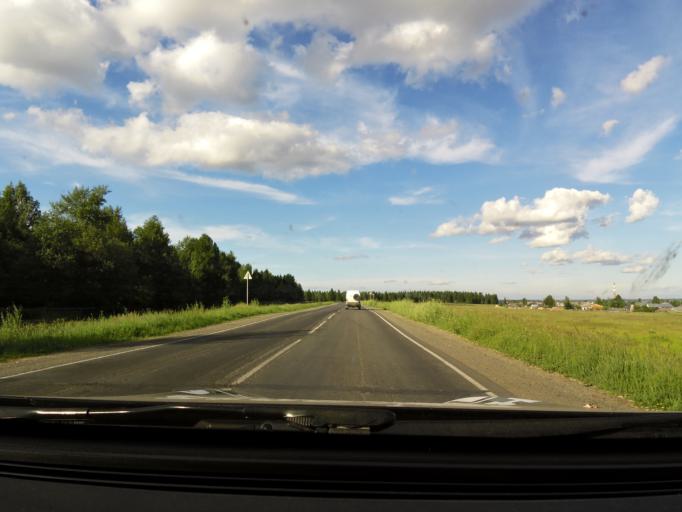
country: RU
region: Kirov
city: Omutninsk
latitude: 58.6912
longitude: 52.1935
